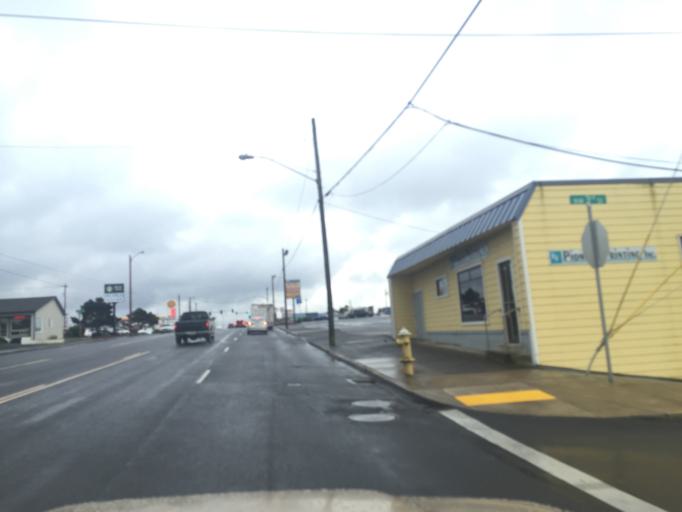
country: US
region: Oregon
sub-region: Lincoln County
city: Newport
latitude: 44.6384
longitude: -124.0532
